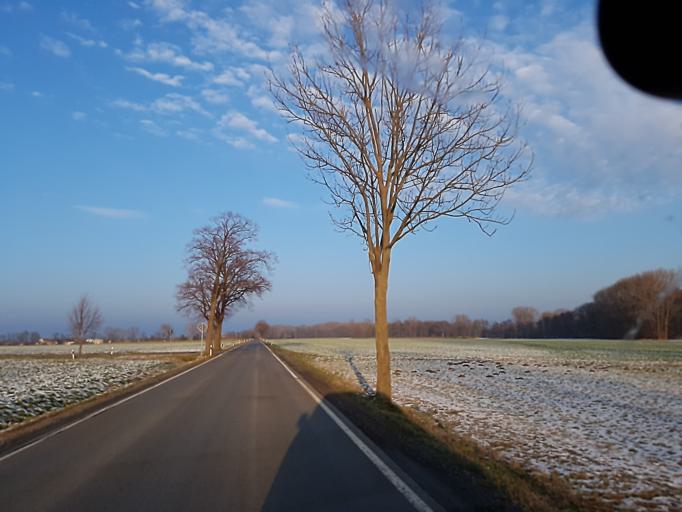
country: DE
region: Saxony
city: Oschatz
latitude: 51.3051
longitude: 13.1710
